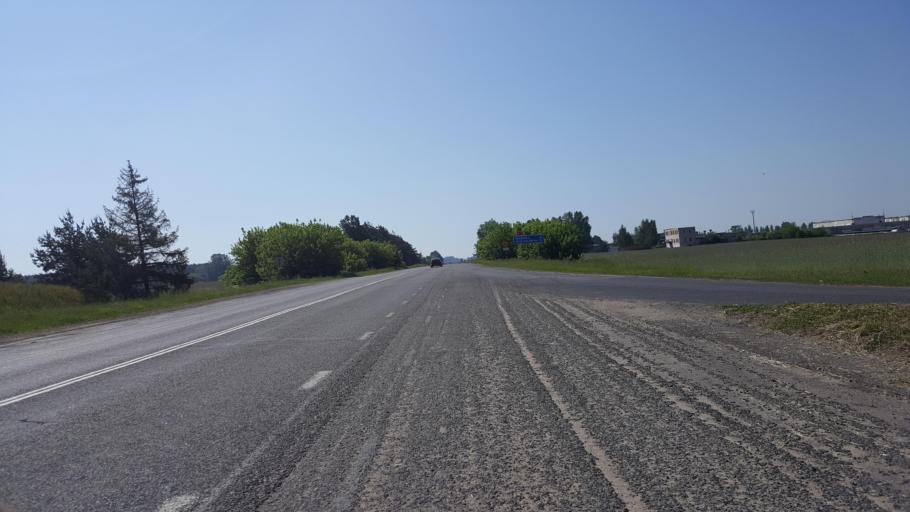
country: BY
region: Brest
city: Kamyanyets
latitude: 52.3395
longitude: 23.9082
